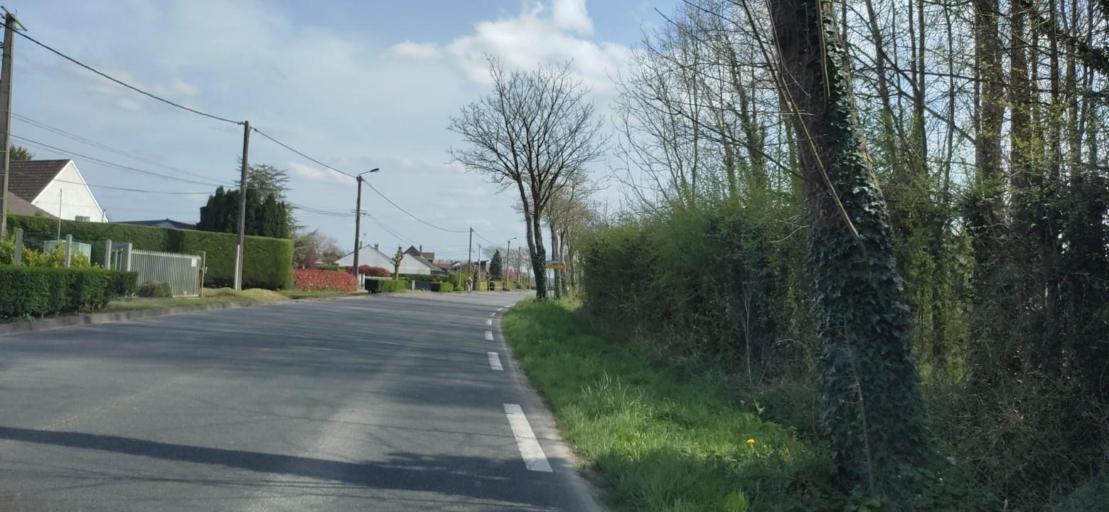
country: FR
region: Nord-Pas-de-Calais
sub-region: Departement du Pas-de-Calais
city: Saint-Josse
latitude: 50.4983
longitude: 1.6973
